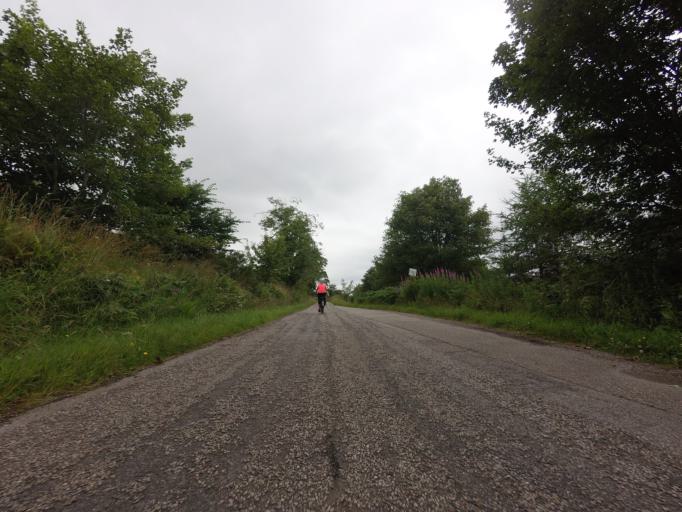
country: GB
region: Scotland
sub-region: Highland
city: Alness
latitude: 57.8969
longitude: -4.3768
